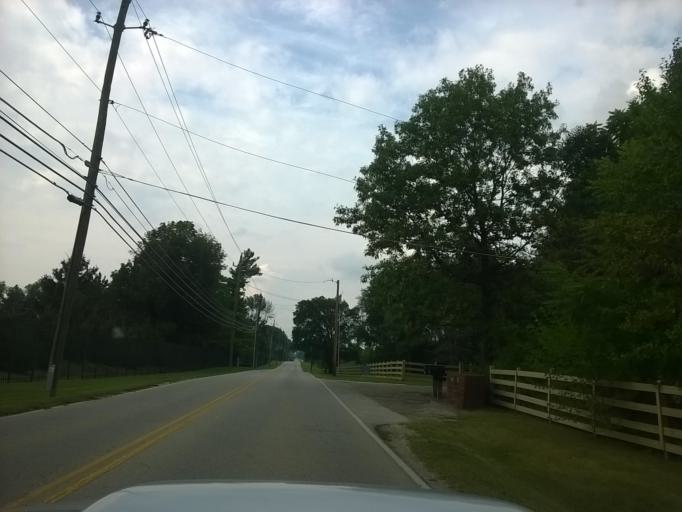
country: US
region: Indiana
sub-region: Marion County
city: Meridian Hills
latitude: 39.9330
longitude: -86.1840
